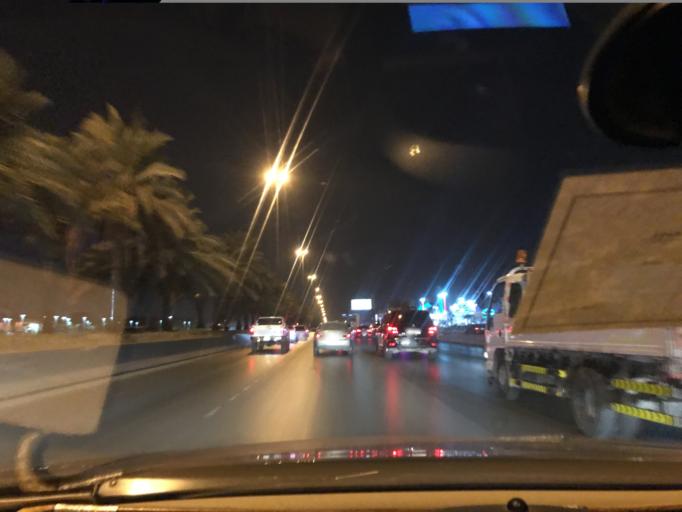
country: SA
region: Ar Riyad
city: Riyadh
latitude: 24.7610
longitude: 46.7383
